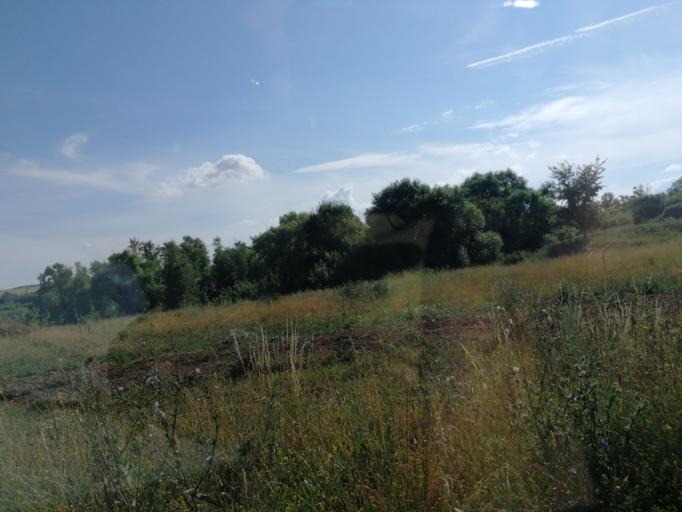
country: RU
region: Tula
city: Tovarkovskiy
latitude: 53.6107
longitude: 38.2716
